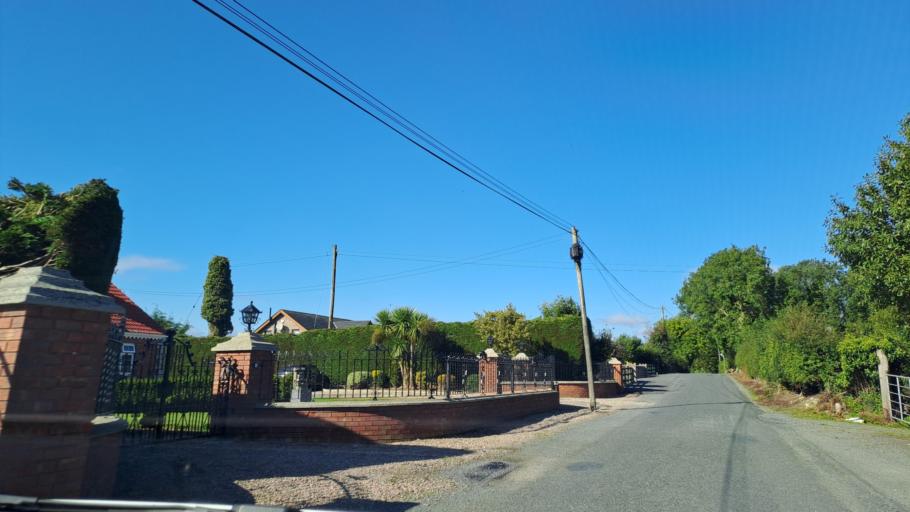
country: IE
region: Ulster
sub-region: County Monaghan
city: Carrickmacross
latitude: 54.0005
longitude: -6.7755
